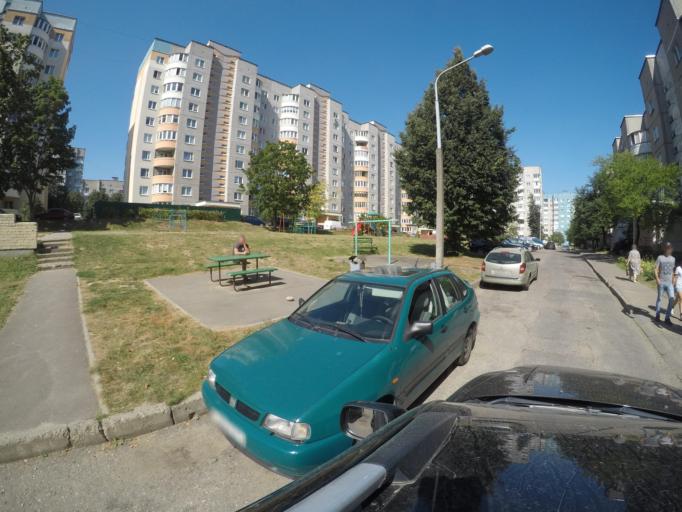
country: BY
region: Grodnenskaya
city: Hrodna
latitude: 53.7022
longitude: 23.8510
